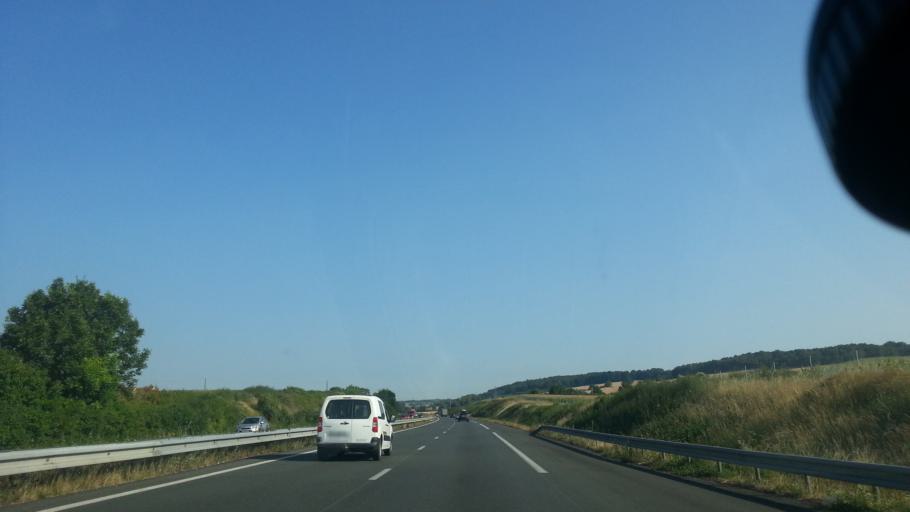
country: FR
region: Poitou-Charentes
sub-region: Departement de la Vienne
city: Antran
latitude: 46.8636
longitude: 0.5248
